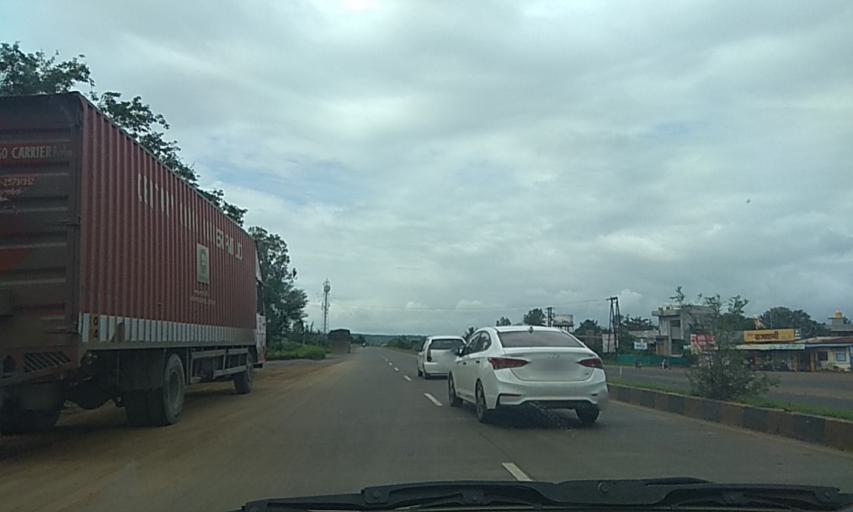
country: IN
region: Maharashtra
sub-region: Kolhapur
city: Kagal
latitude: 16.5678
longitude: 74.3156
